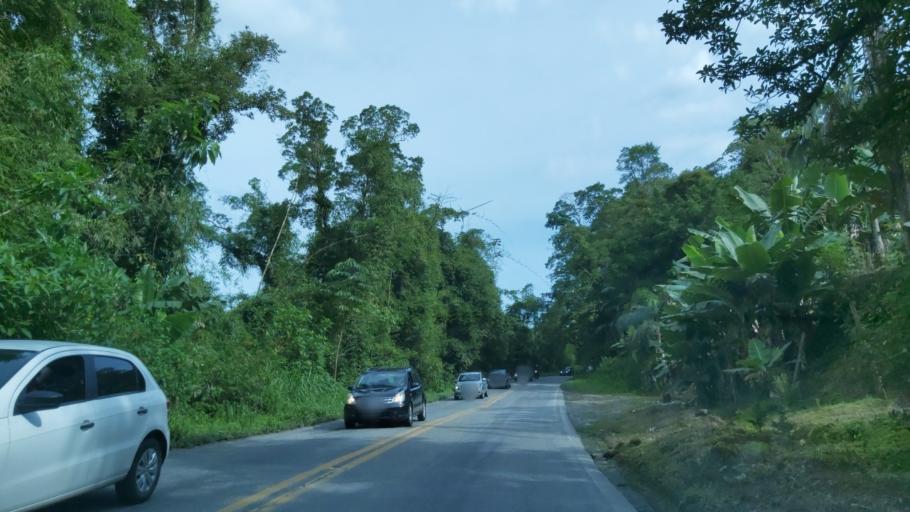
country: BR
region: Sao Paulo
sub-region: Miracatu
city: Miracatu
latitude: -24.0503
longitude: -47.5706
